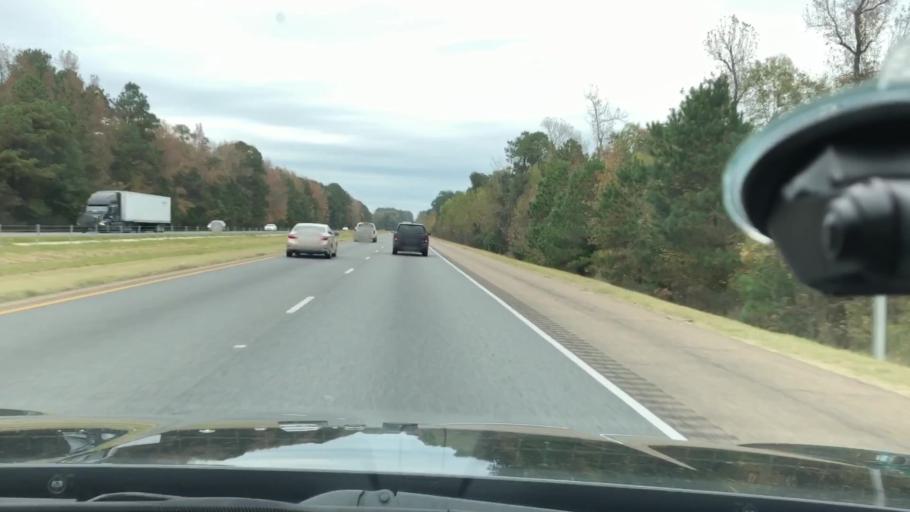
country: US
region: Arkansas
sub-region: Clark County
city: Gurdon
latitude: 33.9108
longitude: -93.2866
